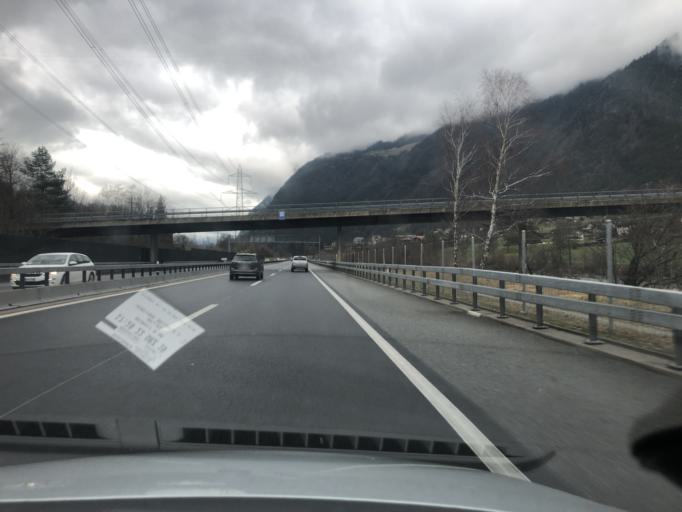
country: CH
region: Uri
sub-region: Uri
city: Silenen
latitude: 46.7938
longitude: 8.6656
